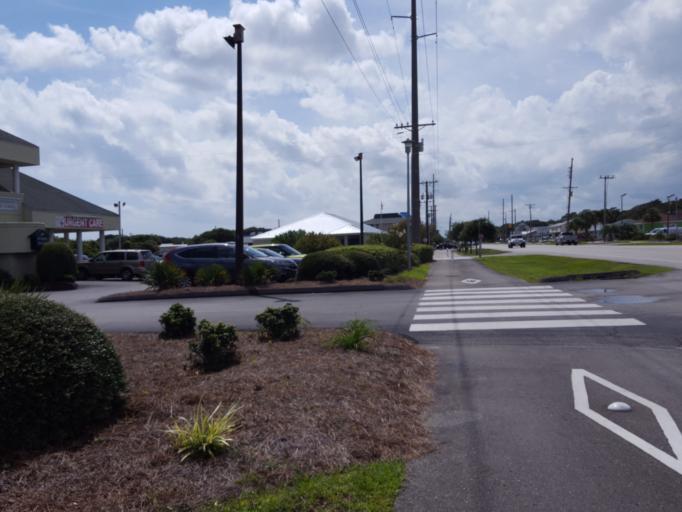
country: US
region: North Carolina
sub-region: Carteret County
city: Cape Carteret
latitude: 34.6653
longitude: -77.0325
